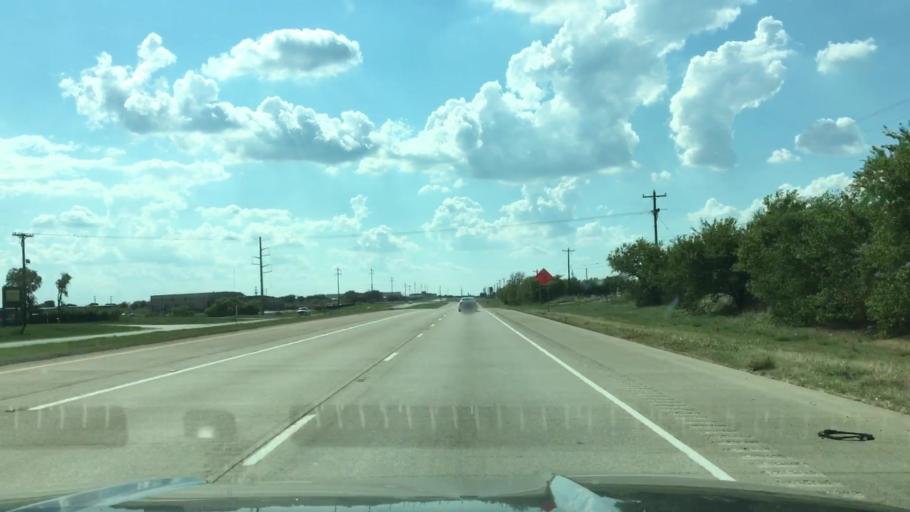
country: US
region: Texas
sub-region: Wise County
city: Rhome
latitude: 33.0370
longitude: -97.4245
